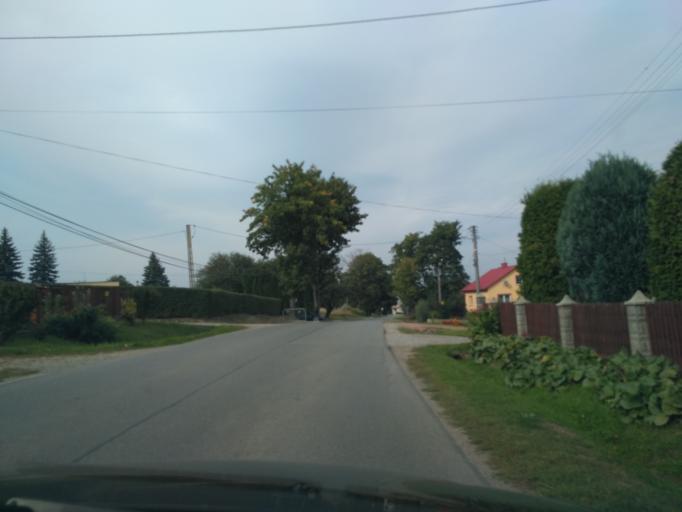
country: PL
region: Subcarpathian Voivodeship
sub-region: Powiat rzeszowski
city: Trzciana
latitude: 50.0564
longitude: 21.8316
